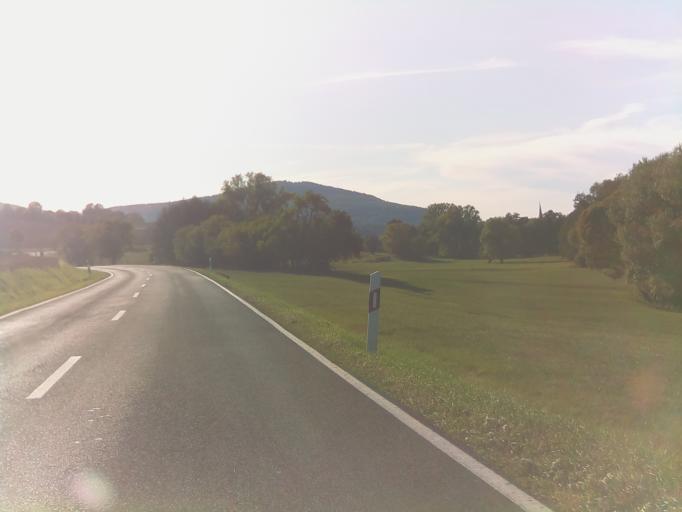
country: DE
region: Thuringia
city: Stepfershausen
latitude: 50.5562
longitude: 10.3034
